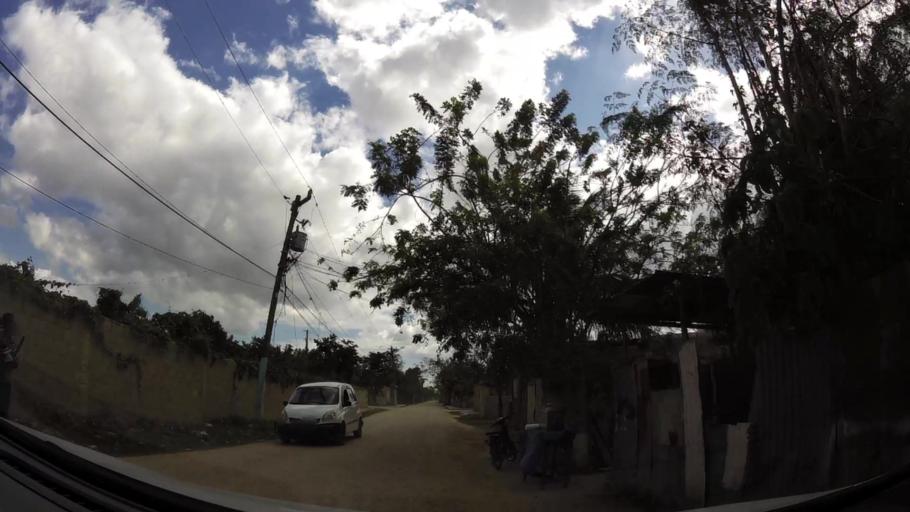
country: DO
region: Santo Domingo
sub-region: Santo Domingo
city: Boca Chica
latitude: 18.4531
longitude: -69.6401
